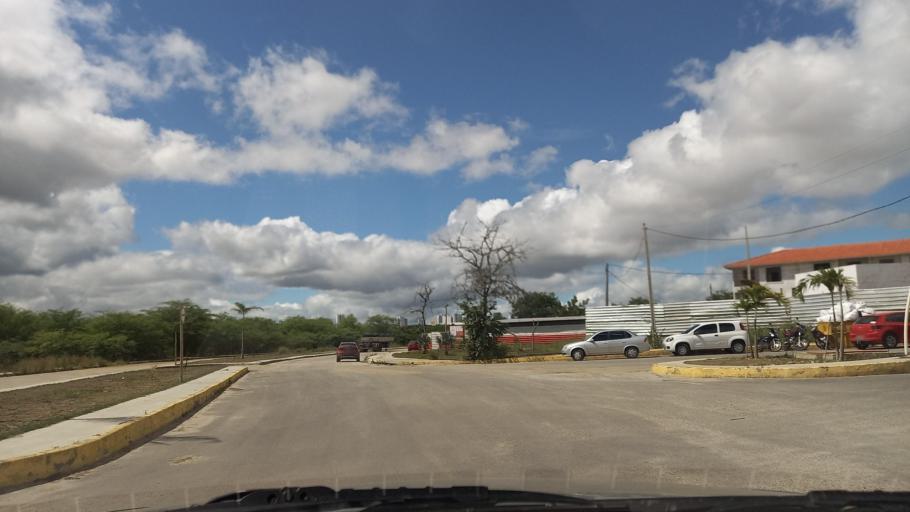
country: BR
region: Pernambuco
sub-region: Caruaru
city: Caruaru
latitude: -8.2448
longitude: -35.9837
